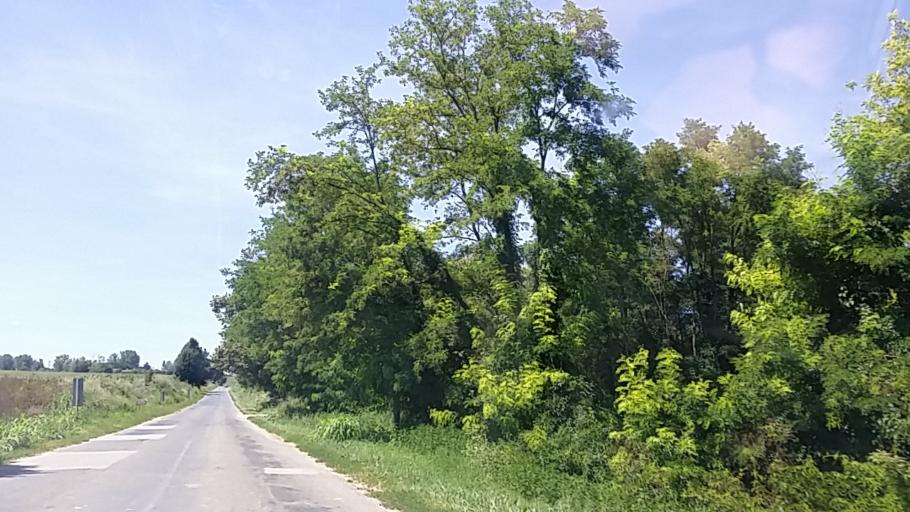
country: HU
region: Somogy
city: Karad
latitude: 46.6795
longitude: 17.8757
